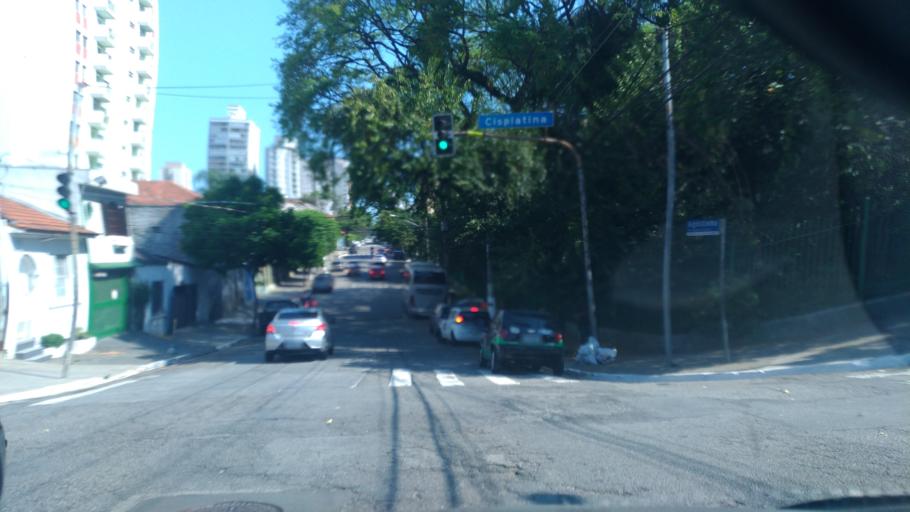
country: BR
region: Sao Paulo
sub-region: Sao Paulo
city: Sao Paulo
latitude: -23.5881
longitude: -46.6040
